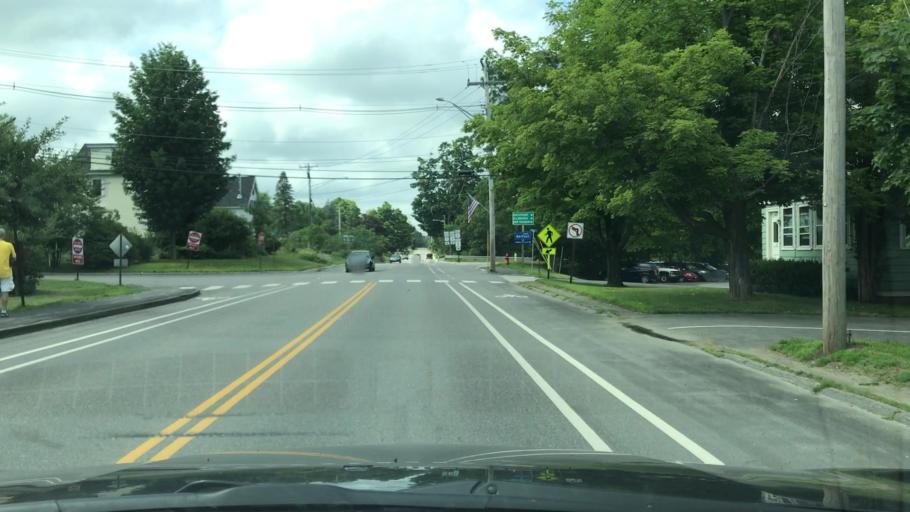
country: US
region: Maine
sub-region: Waldo County
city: Belfast
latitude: 44.4309
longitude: -69.0144
